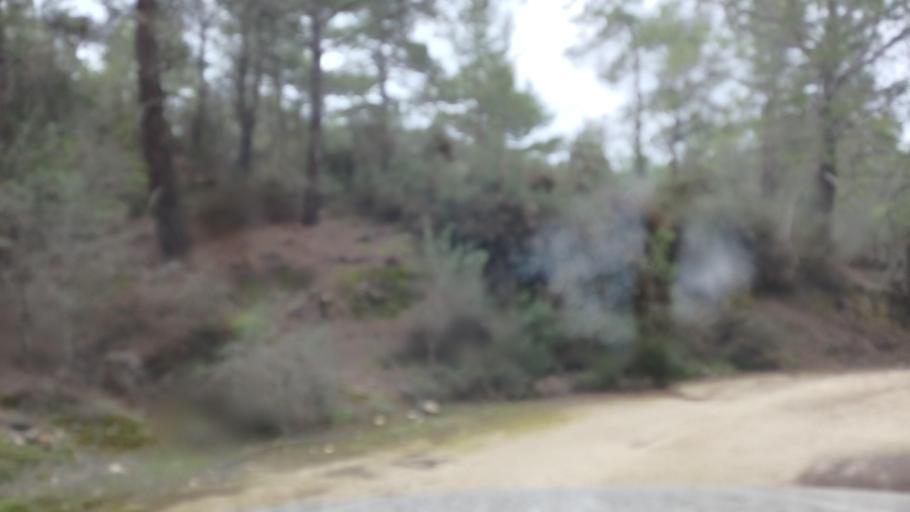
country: CY
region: Limassol
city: Pachna
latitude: 34.7731
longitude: 32.6941
